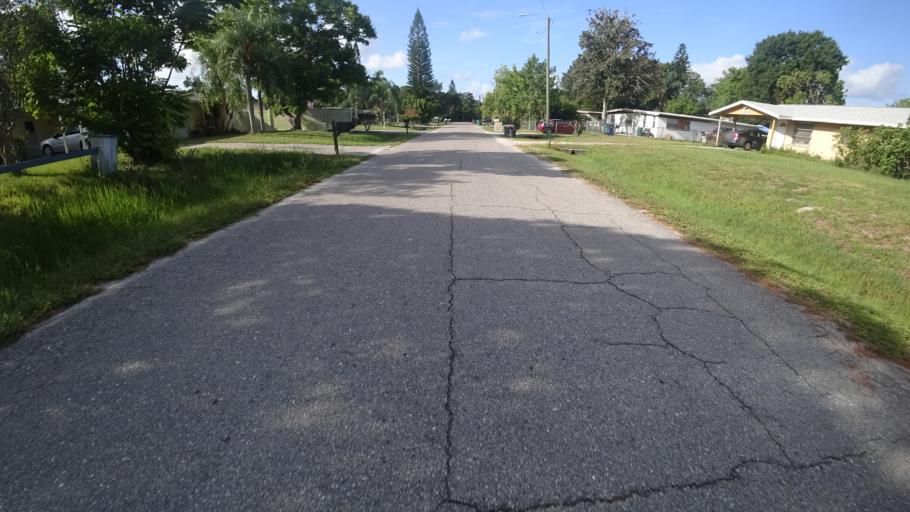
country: US
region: Florida
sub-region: Manatee County
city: Whitfield
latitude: 27.4382
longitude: -82.5636
